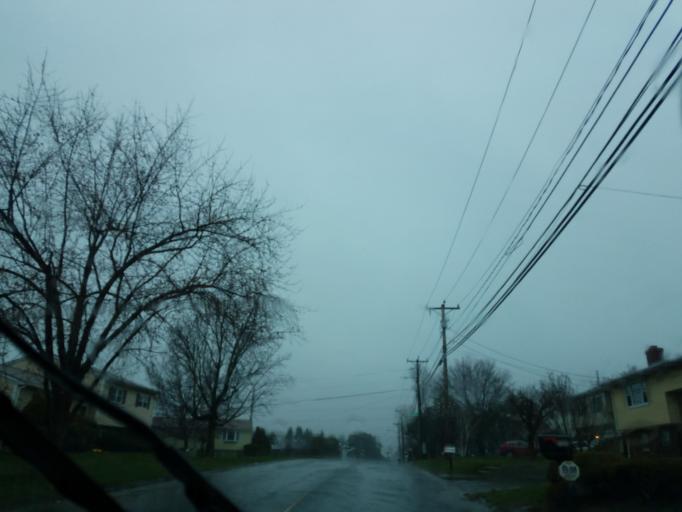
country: US
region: Connecticut
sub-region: New Haven County
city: Waterbury
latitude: 41.5266
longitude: -73.0657
